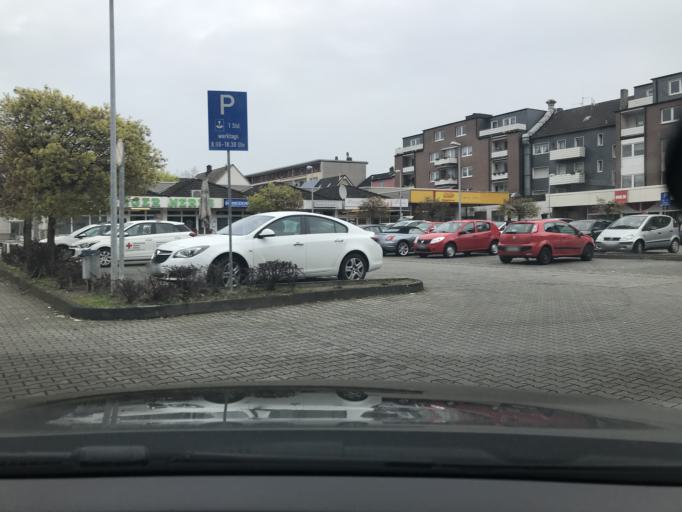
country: DE
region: North Rhine-Westphalia
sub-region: Regierungsbezirk Dusseldorf
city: Dinslaken
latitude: 51.5275
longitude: 6.7416
